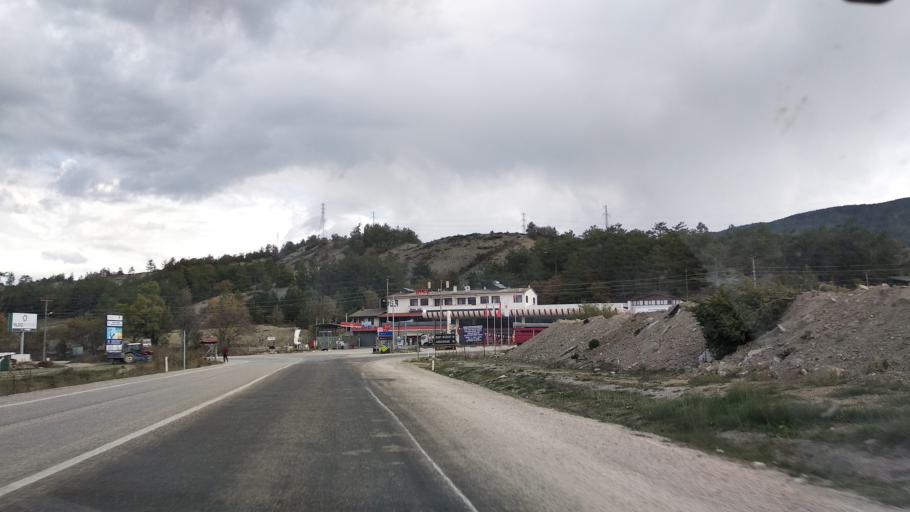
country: TR
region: Bolu
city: Mudurnu
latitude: 40.4897
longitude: 31.2008
